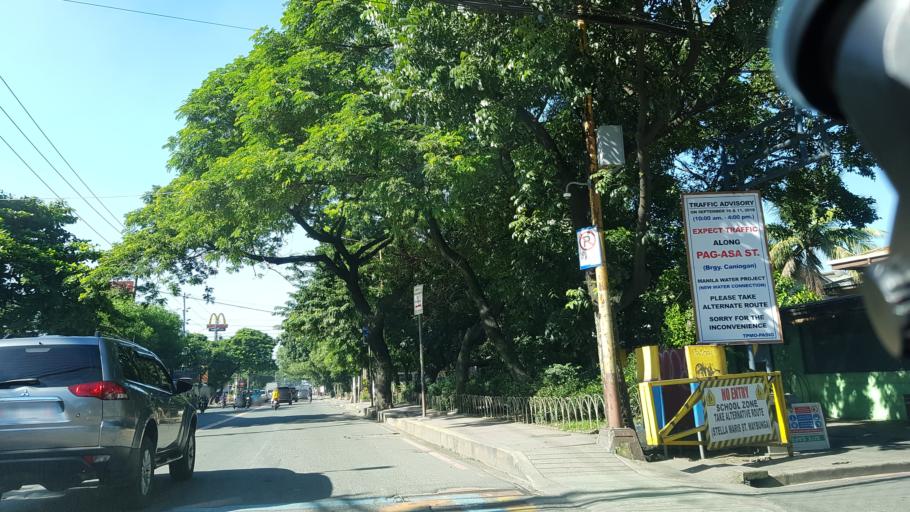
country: PH
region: Metro Manila
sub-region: Pasig
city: Pasig City
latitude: 14.5728
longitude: 121.0833
